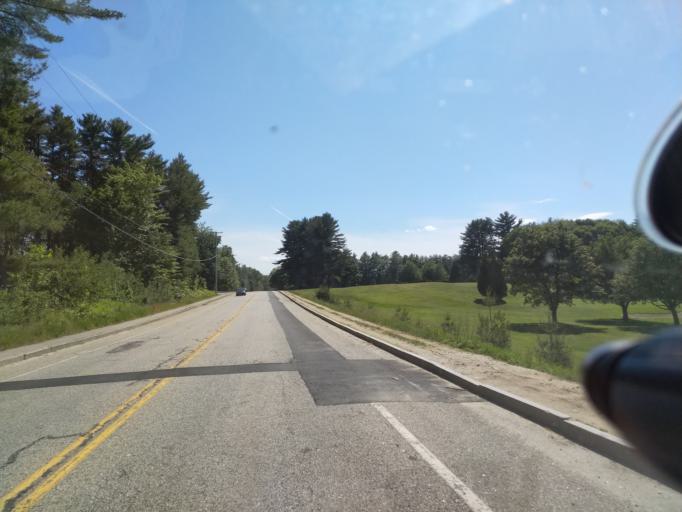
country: US
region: Maine
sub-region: Cumberland County
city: Westbrook
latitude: 43.7118
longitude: -70.3119
